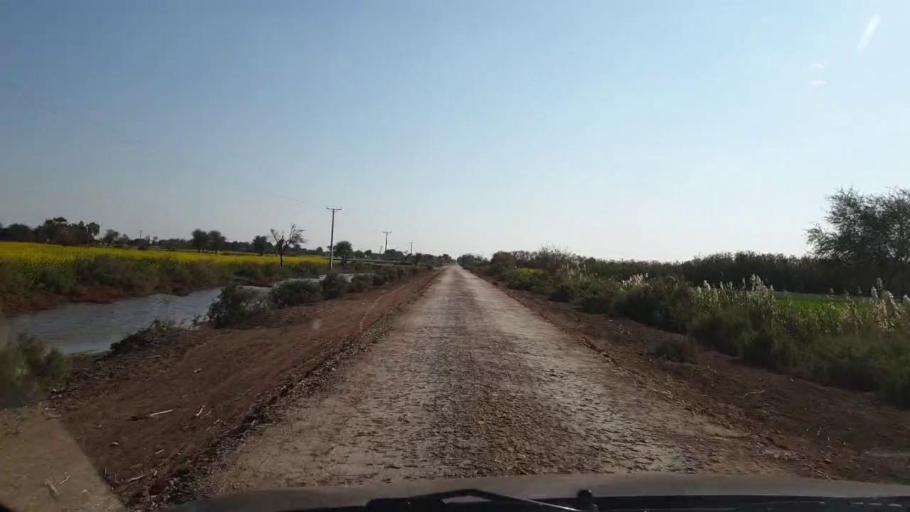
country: PK
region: Sindh
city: Sinjhoro
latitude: 25.9913
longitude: 68.8394
